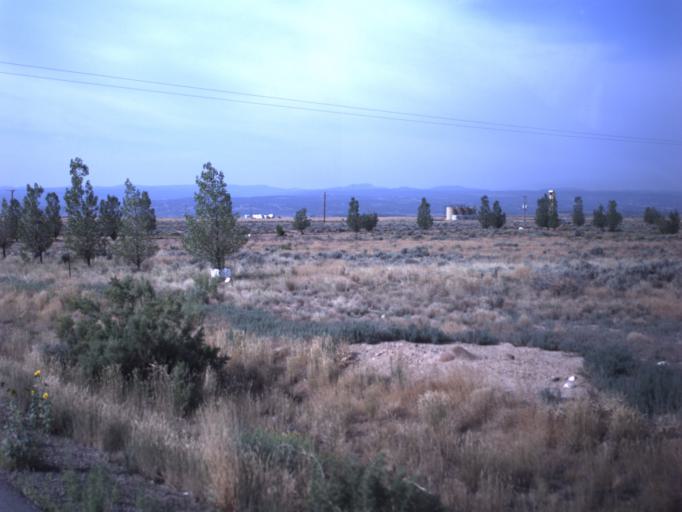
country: US
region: Utah
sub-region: Duchesne County
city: Duchesne
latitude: 40.2196
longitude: -110.3893
